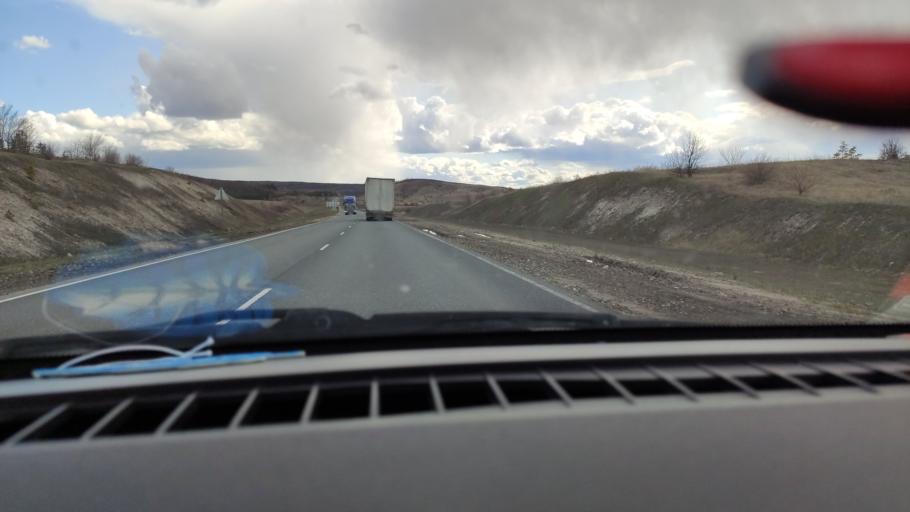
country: RU
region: Saratov
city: Alekseyevka
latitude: 52.3818
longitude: 47.9730
